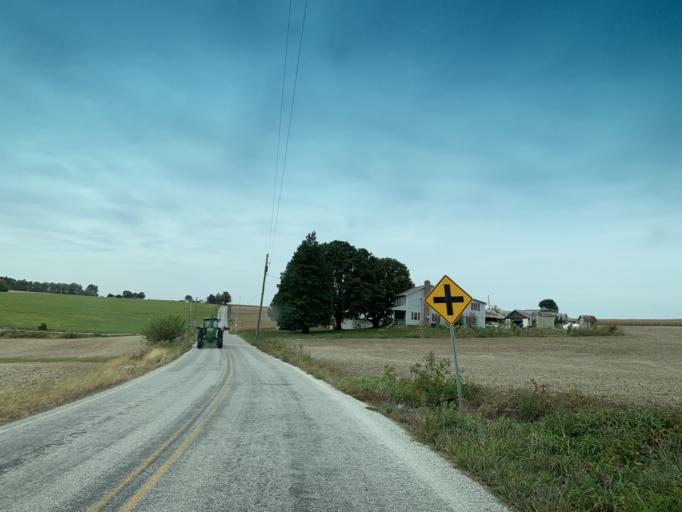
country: US
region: Pennsylvania
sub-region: York County
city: Stewartstown
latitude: 39.8041
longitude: -76.5166
